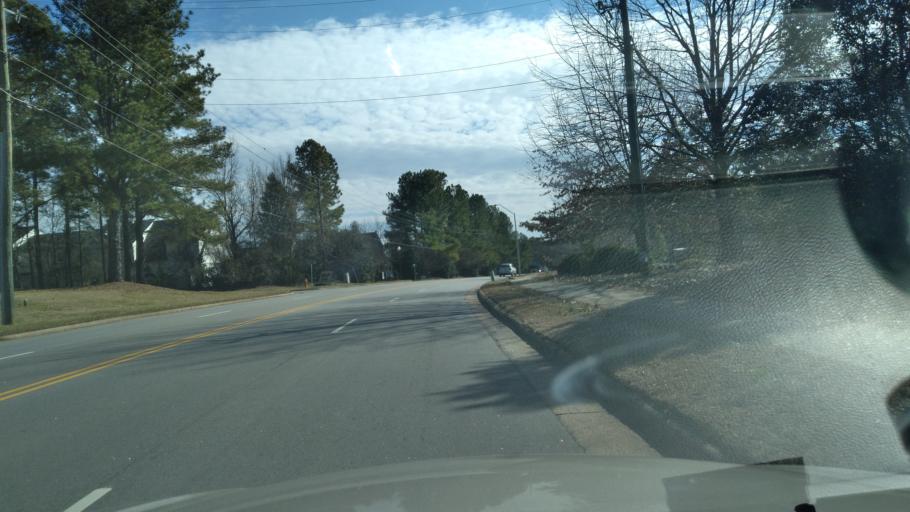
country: US
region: North Carolina
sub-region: Wake County
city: Garner
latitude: 35.6973
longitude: -78.6167
